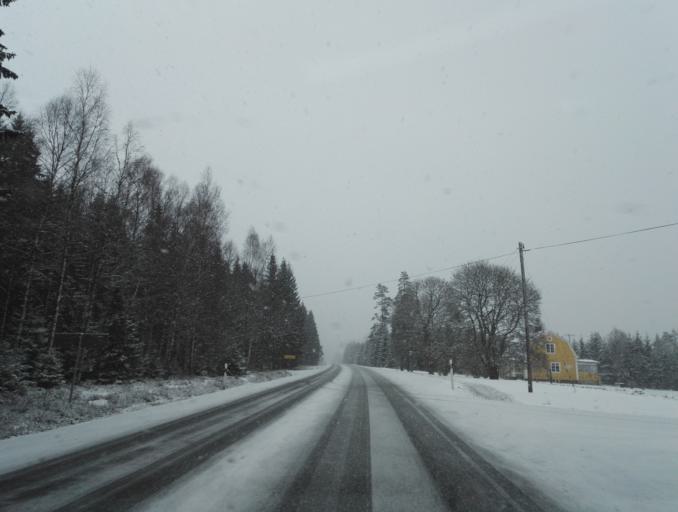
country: SE
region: Kronoberg
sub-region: Uppvidinge Kommun
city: Lenhovda
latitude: 57.0398
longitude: 15.2092
